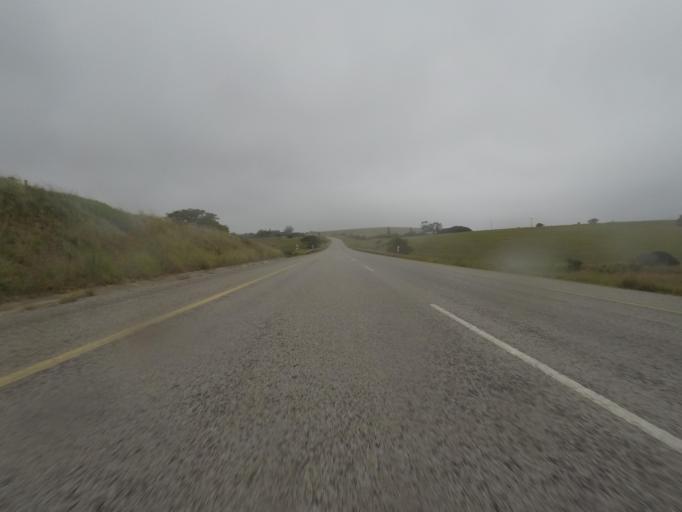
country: ZA
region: Eastern Cape
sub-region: Cacadu District Municipality
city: Grahamstown
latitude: -33.6334
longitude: 26.3166
